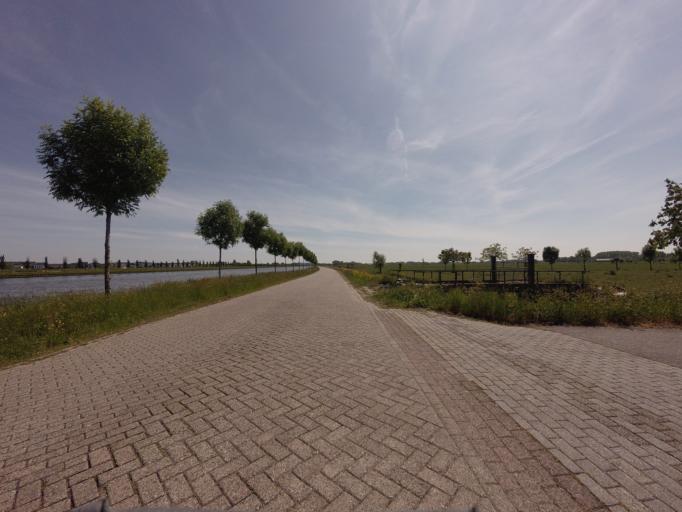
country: NL
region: Utrecht
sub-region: Gemeente Houten
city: Houten
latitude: 52.0115
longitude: 5.1546
